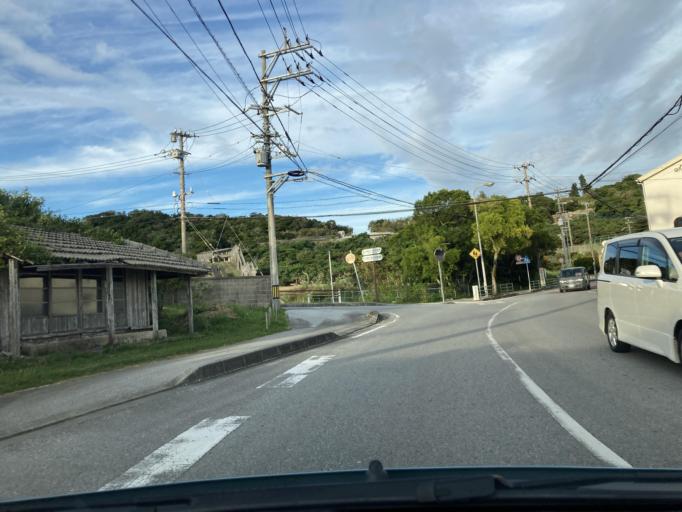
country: JP
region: Okinawa
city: Tomigusuku
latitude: 26.1510
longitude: 127.7026
